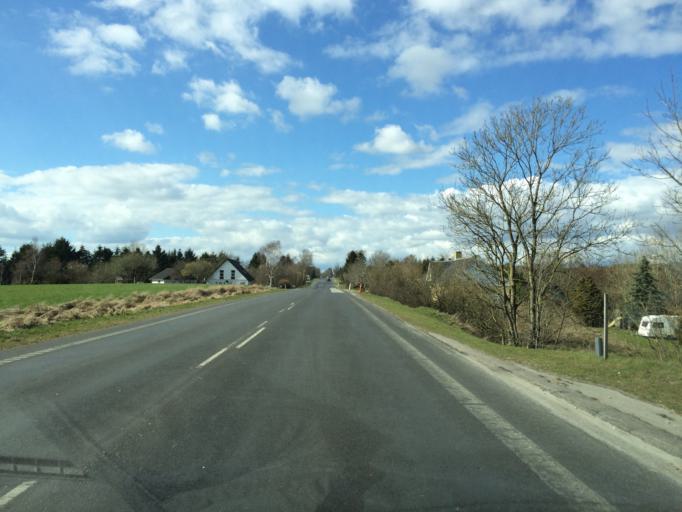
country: DK
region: South Denmark
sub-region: Assens Kommune
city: Arup
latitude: 55.4237
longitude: 10.0293
